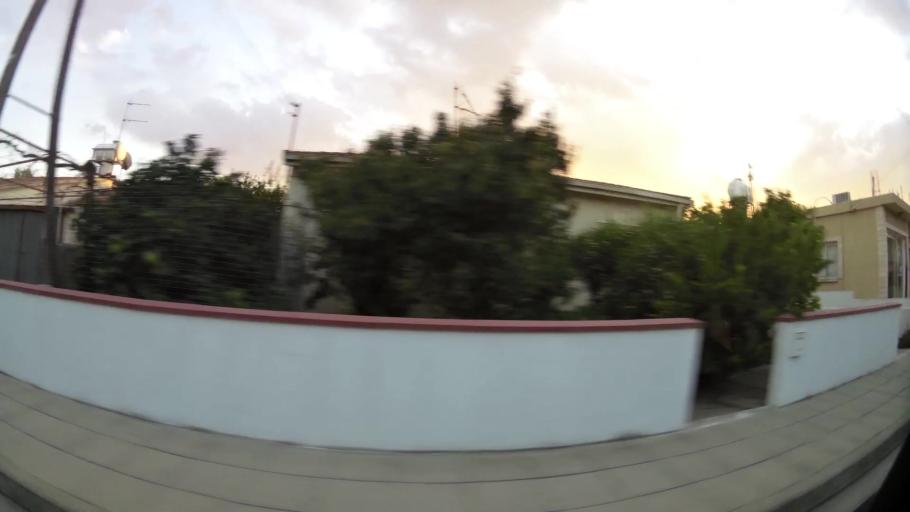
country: CY
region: Larnaka
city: Dhromolaxia
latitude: 34.8702
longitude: 33.5871
